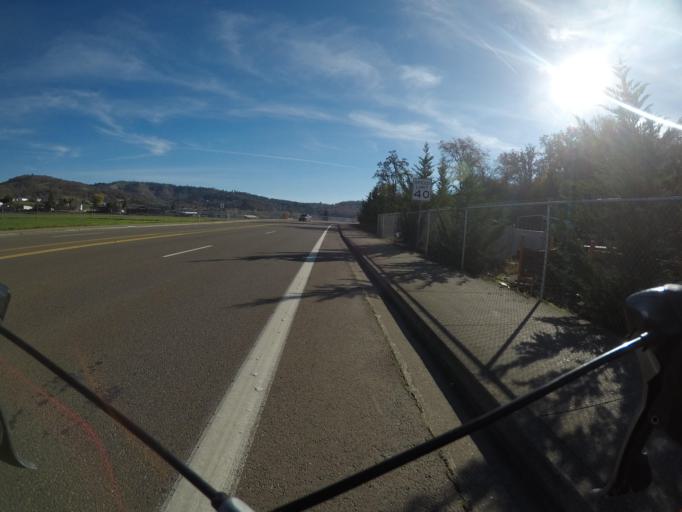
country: US
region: Oregon
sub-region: Douglas County
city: Roseburg
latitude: 43.2329
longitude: -123.3585
